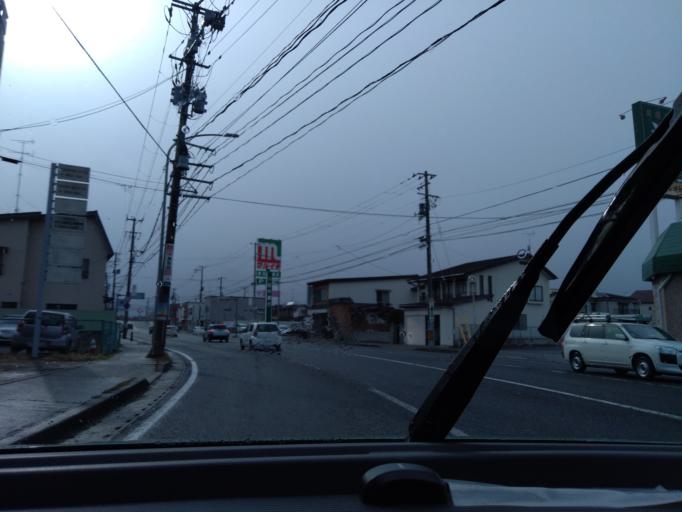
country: JP
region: Iwate
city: Morioka-shi
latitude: 39.7049
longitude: 141.1279
